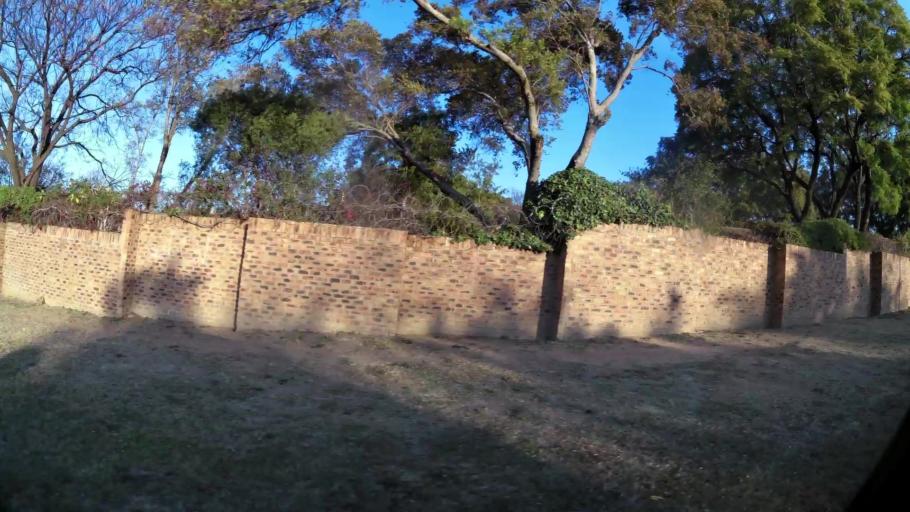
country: ZA
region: Gauteng
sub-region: City of Johannesburg Metropolitan Municipality
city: Diepsloot
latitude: -26.0370
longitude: 27.9778
